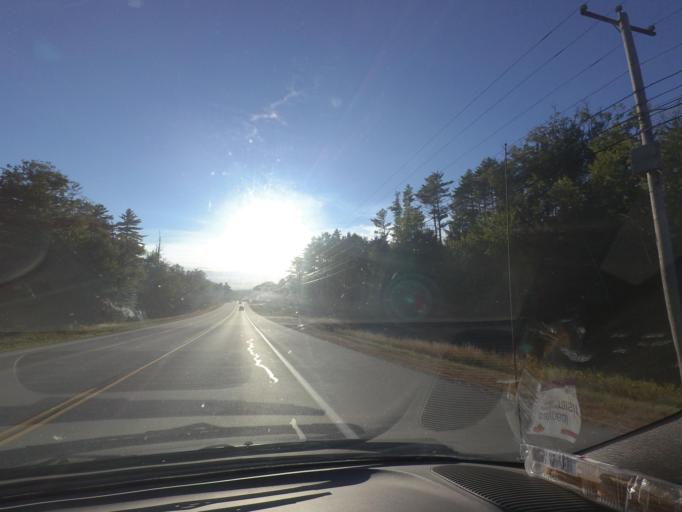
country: US
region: New Hampshire
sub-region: Merrimack County
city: Chichester
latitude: 43.2468
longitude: -71.4293
